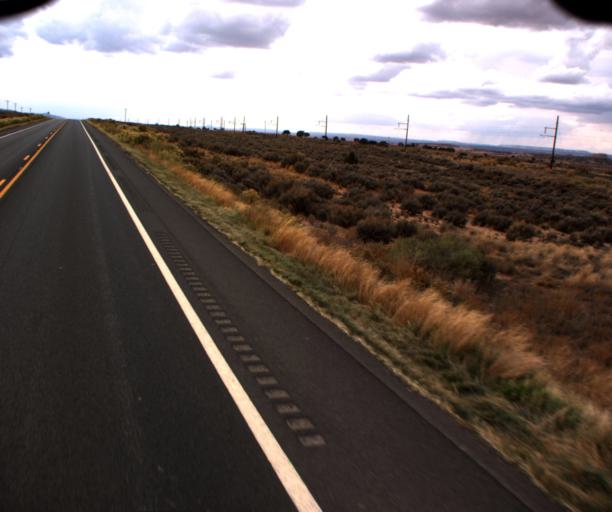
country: US
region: Arizona
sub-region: Navajo County
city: Kayenta
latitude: 36.5211
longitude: -110.5859
